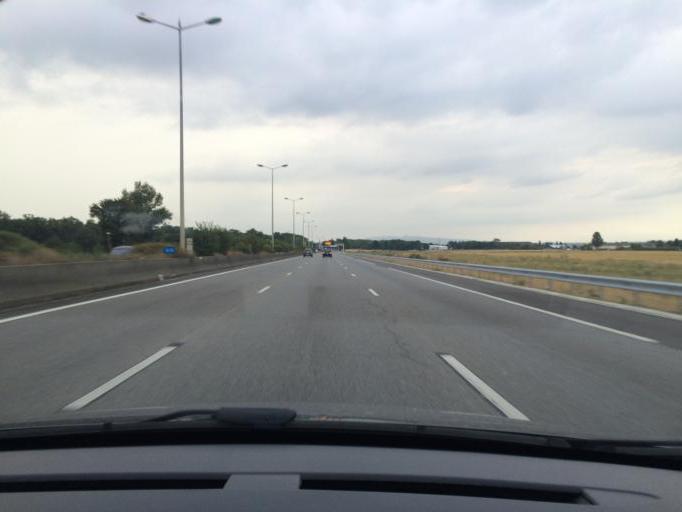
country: FR
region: Rhone-Alpes
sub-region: Departement du Rhone
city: Saint-Priest
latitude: 45.7136
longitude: 4.9457
